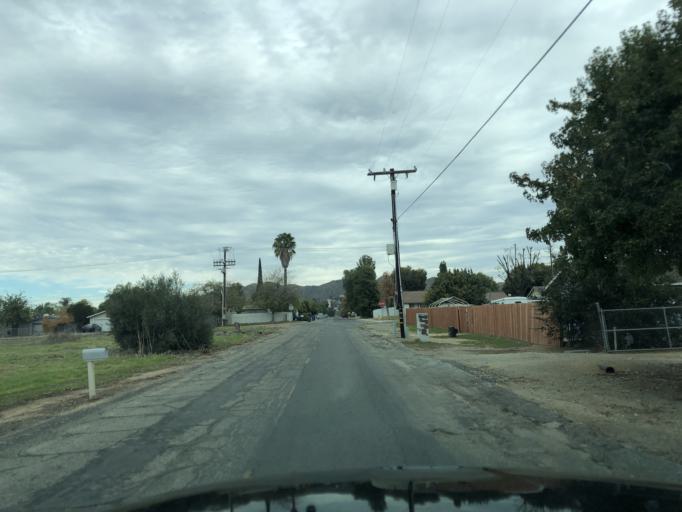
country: US
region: California
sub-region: Riverside County
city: Wildomar
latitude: 33.6188
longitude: -117.2711
